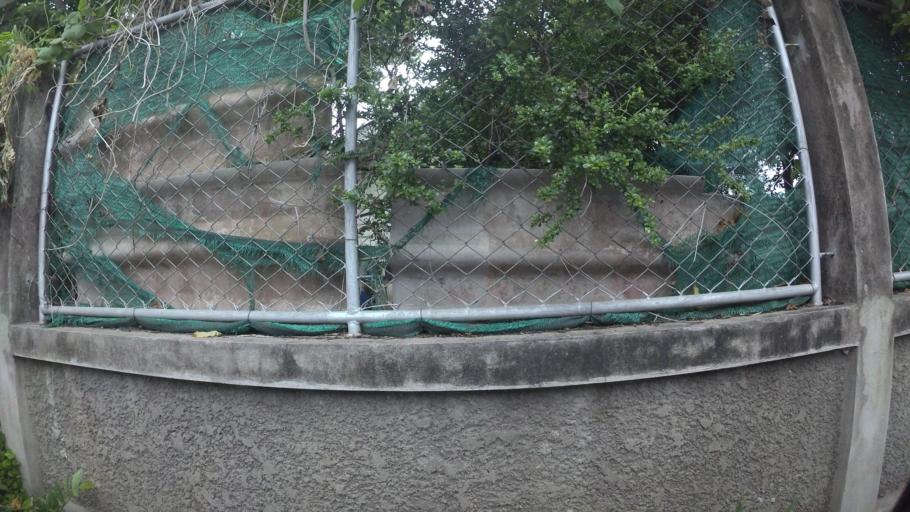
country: TH
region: Chon Buri
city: Sattahip
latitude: 12.6955
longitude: 100.8968
